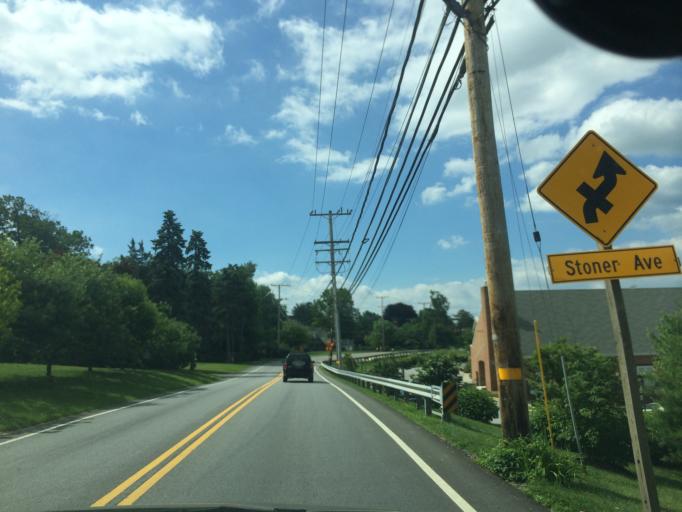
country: US
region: Maryland
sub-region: Carroll County
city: Westminster
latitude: 39.5605
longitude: -76.9871
